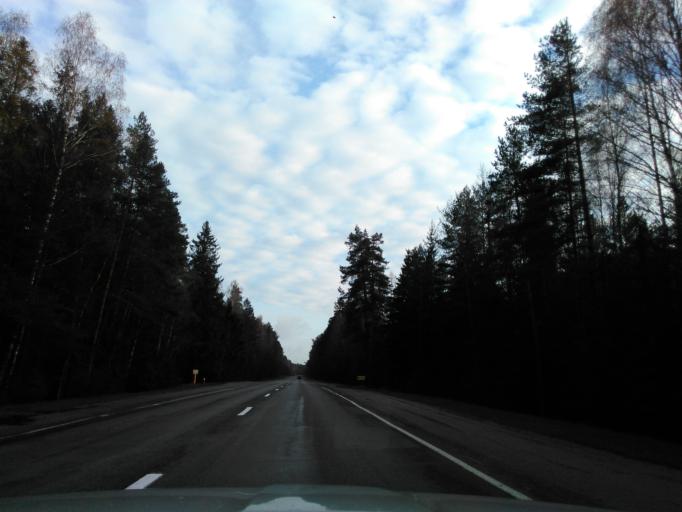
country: BY
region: Minsk
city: Plyeshchanitsy
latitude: 54.3673
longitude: 27.8835
